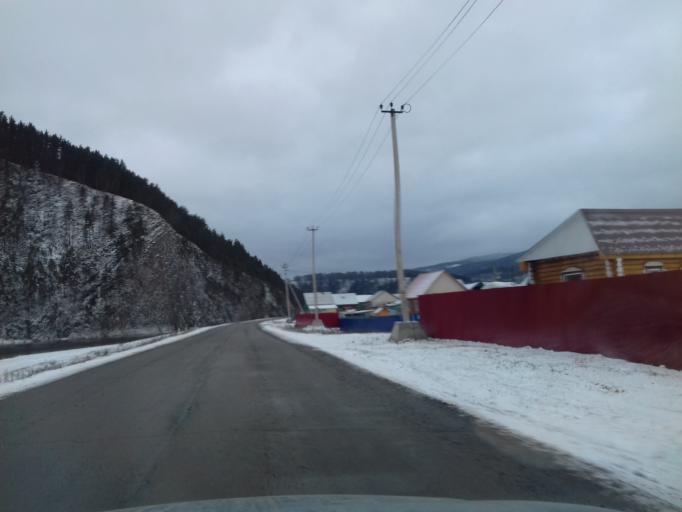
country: RU
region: Bashkortostan
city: Starosubkhangulovo
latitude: 53.0968
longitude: 57.4447
